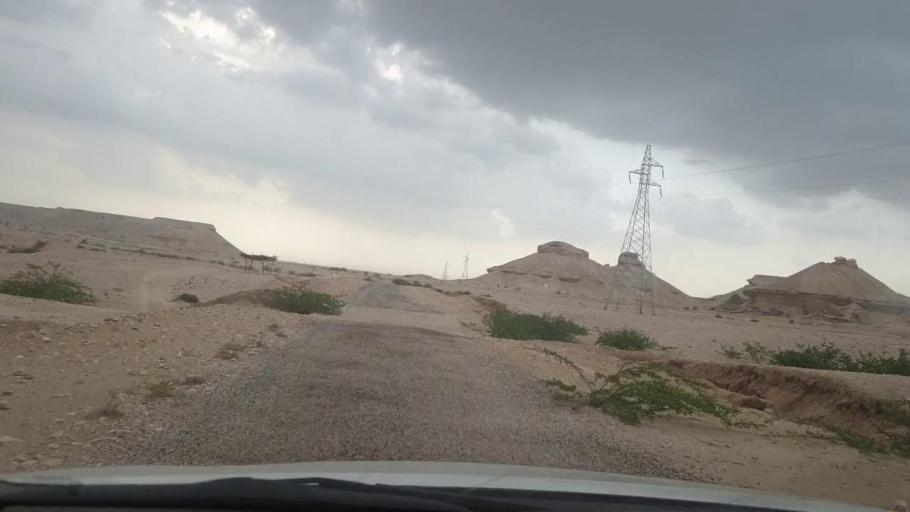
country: PK
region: Sindh
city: Khairpur
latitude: 27.4704
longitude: 68.8951
